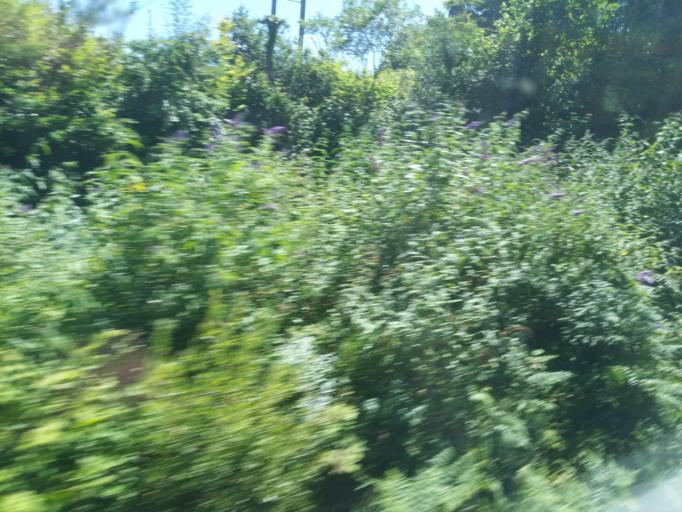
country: GB
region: England
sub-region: Cornwall
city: St Austell
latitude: 50.3420
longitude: -4.8159
